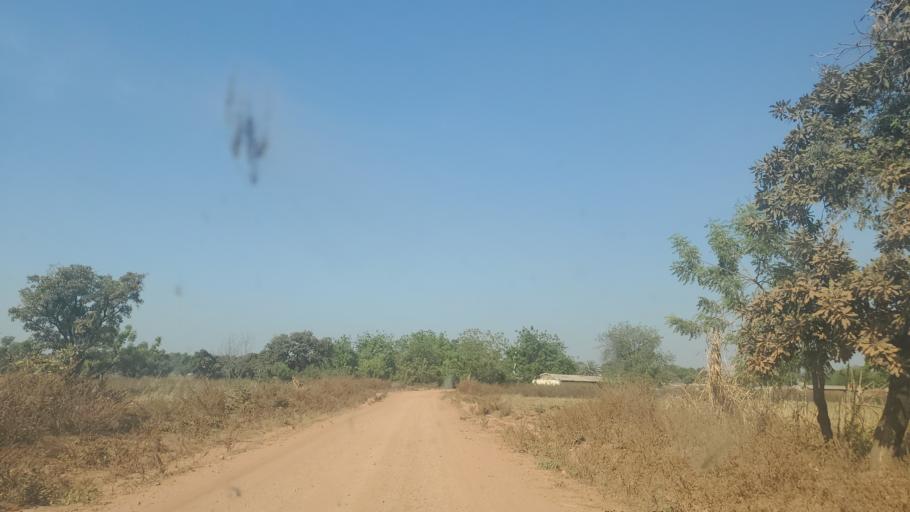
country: NG
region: Niger
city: Badeggi
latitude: 9.1248
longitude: 6.1934
